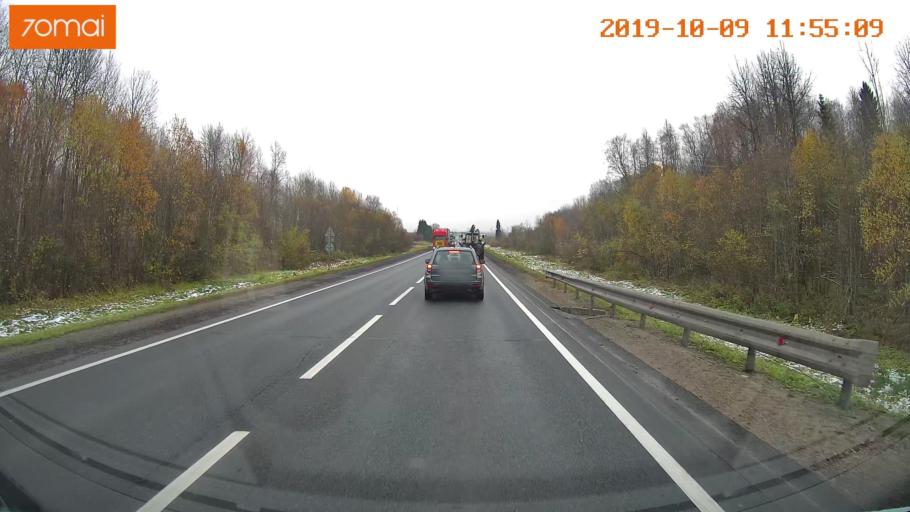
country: RU
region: Vologda
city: Gryazovets
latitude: 58.7511
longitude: 40.2847
